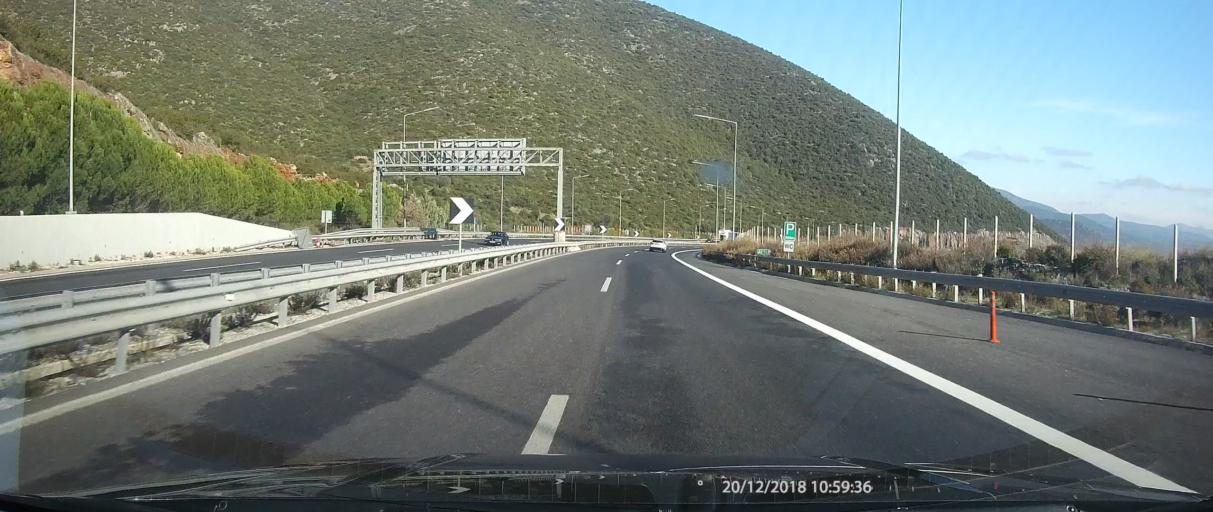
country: GR
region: Peloponnese
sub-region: Nomos Korinthias
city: Nemea
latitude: 37.7004
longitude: 22.5344
